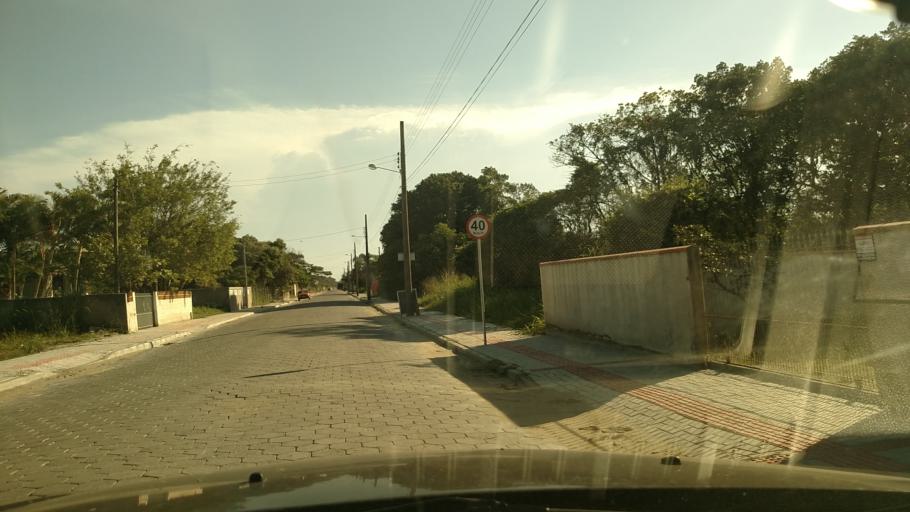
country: BR
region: Santa Catarina
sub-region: Porto Belo
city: Porto Belo
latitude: -27.1737
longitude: -48.5040
